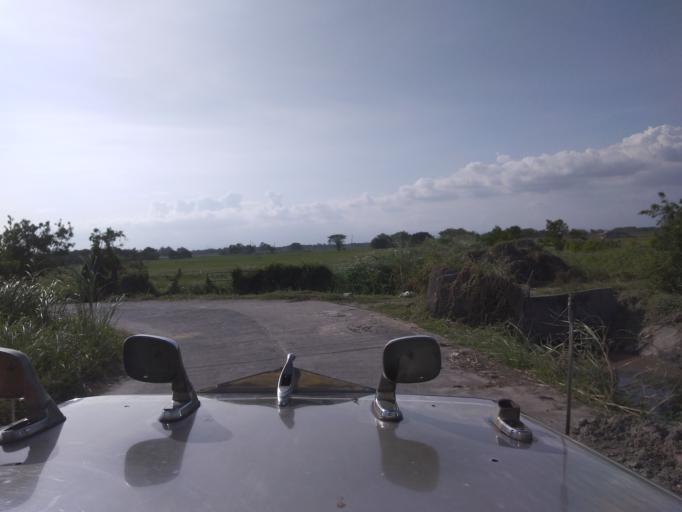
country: PH
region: Central Luzon
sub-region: Province of Pampanga
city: San Patricio
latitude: 15.0987
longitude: 120.6985
